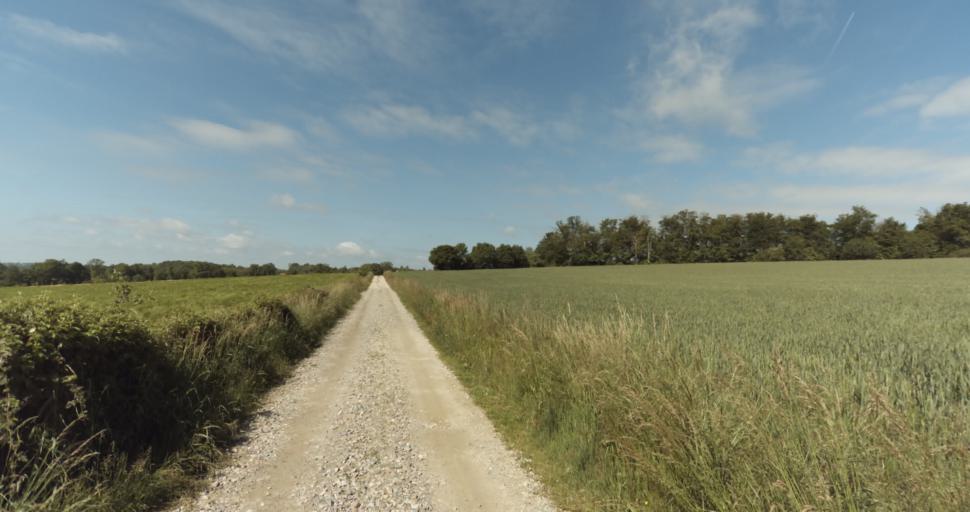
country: FR
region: Limousin
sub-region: Departement de la Haute-Vienne
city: Solignac
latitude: 45.7215
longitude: 1.2610
